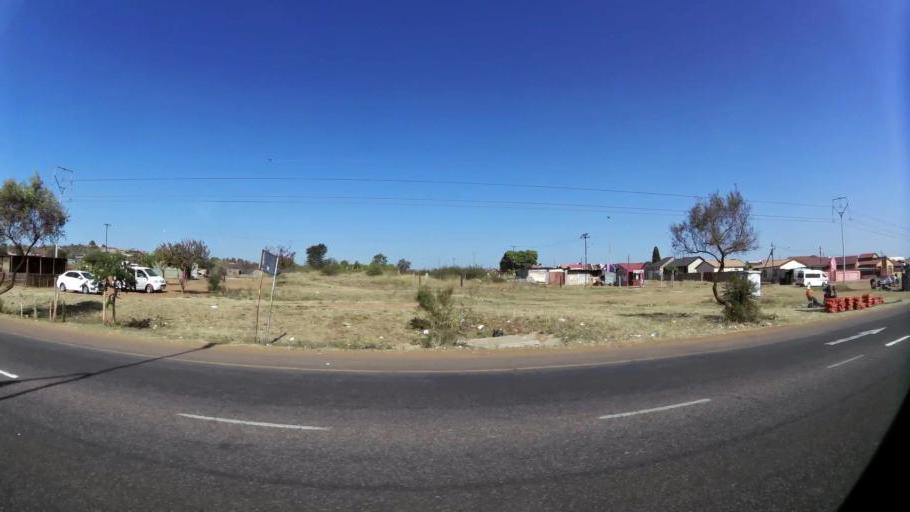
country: ZA
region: Gauteng
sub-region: City of Tshwane Metropolitan Municipality
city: Mabopane
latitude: -25.5220
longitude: 28.0938
